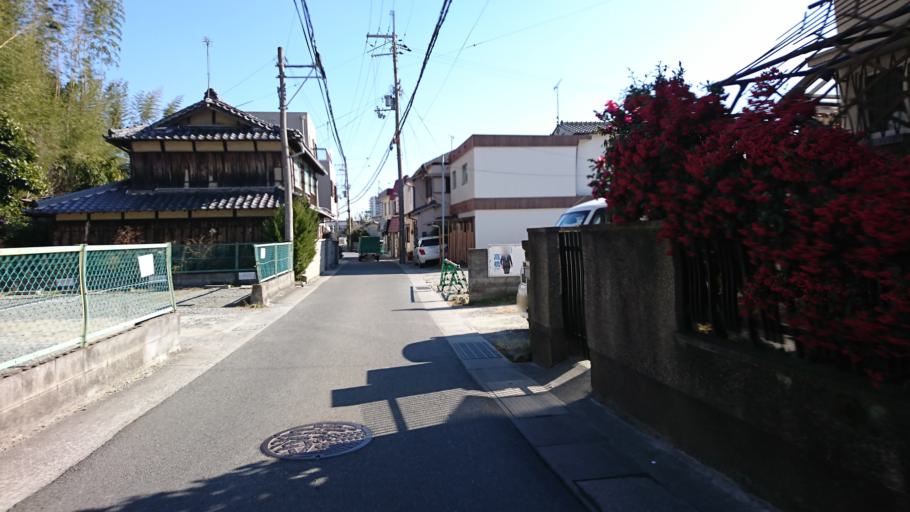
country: JP
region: Hyogo
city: Kakogawacho-honmachi
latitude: 34.7918
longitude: 134.7986
